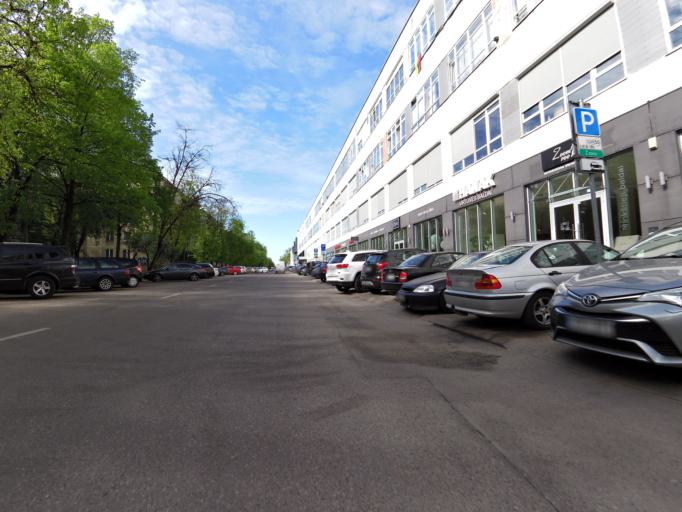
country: LT
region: Vilnius County
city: Naujamiestis
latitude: 54.6744
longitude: 25.2653
